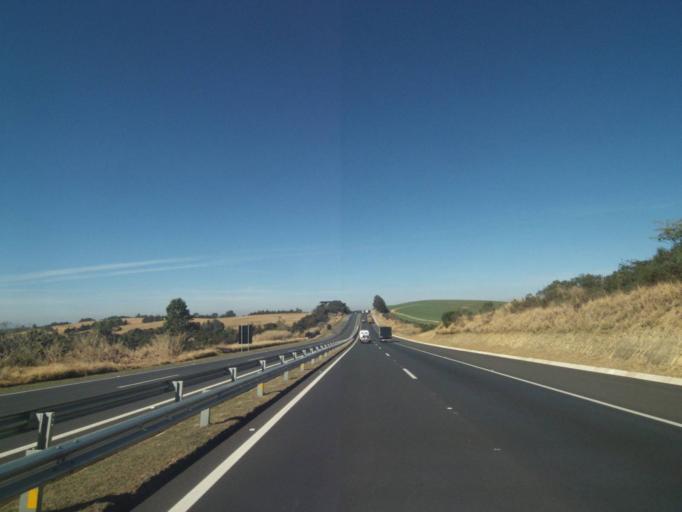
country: BR
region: Parana
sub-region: Carambei
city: Carambei
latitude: -24.8654
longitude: -50.4465
